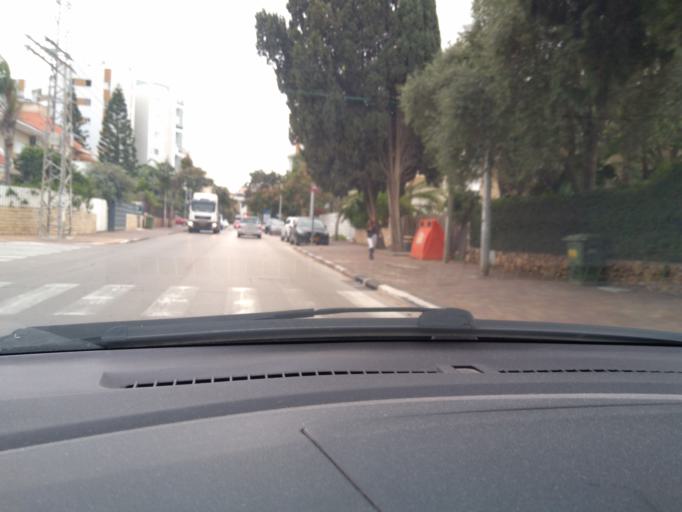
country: IL
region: Central District
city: Netanya
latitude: 32.3434
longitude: 34.8622
